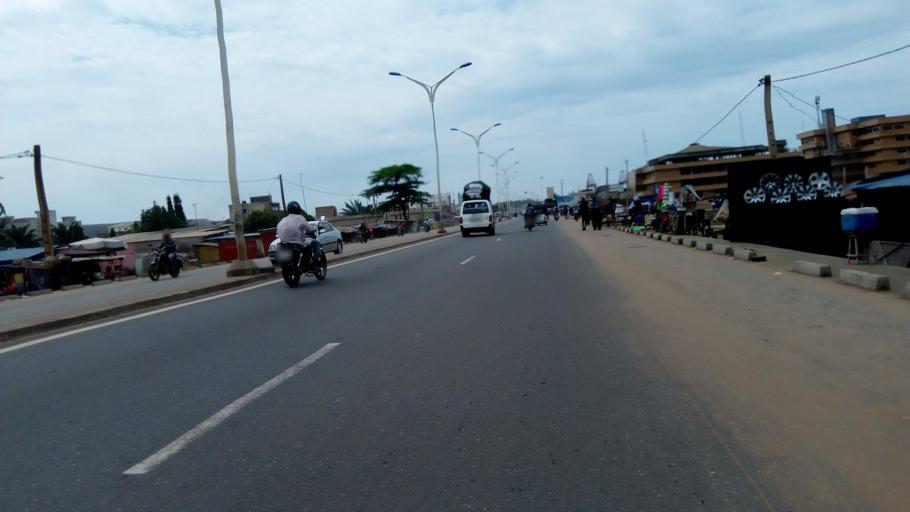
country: TG
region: Maritime
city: Lome
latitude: 6.1612
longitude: 1.2843
